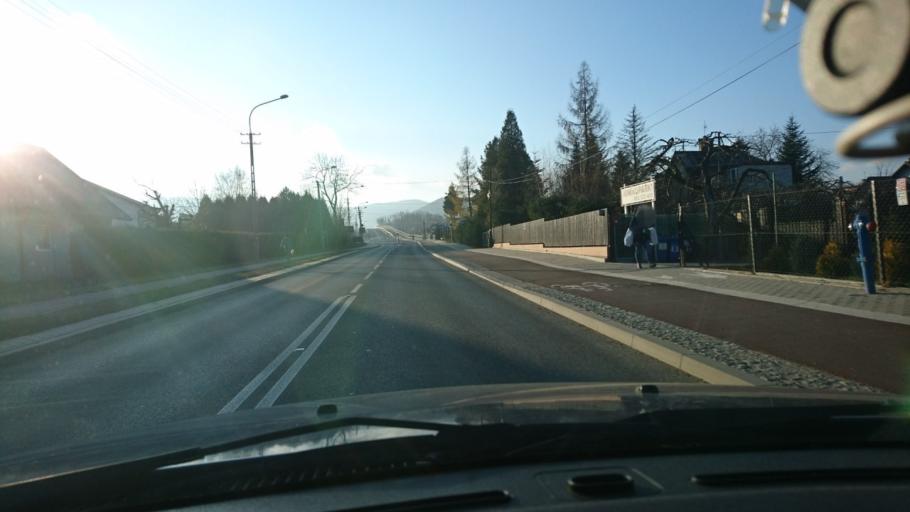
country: PL
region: Silesian Voivodeship
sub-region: Powiat bielski
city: Jaworze
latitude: 49.8147
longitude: 18.9751
